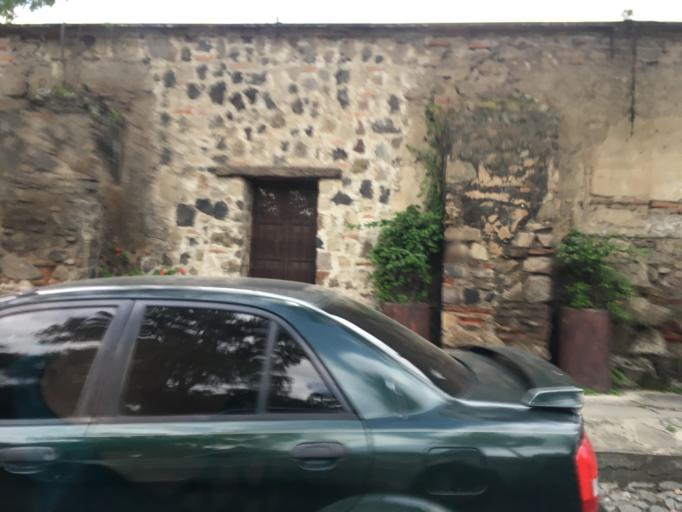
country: GT
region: Sacatepequez
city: Antigua Guatemala
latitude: 14.5548
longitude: -90.7400
